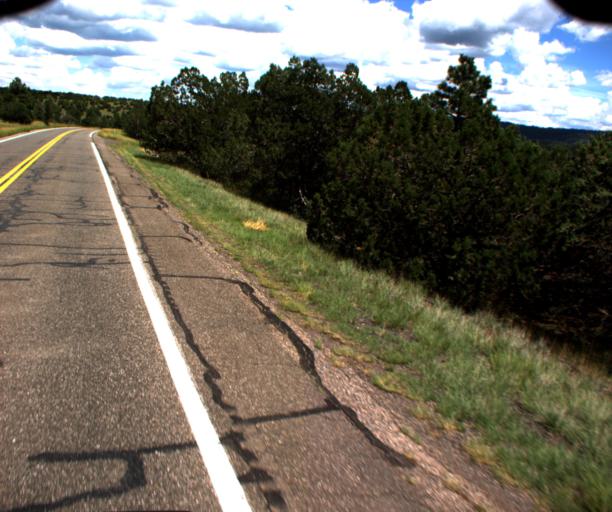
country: US
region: Arizona
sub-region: Gila County
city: Pine
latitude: 34.5122
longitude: -111.5412
